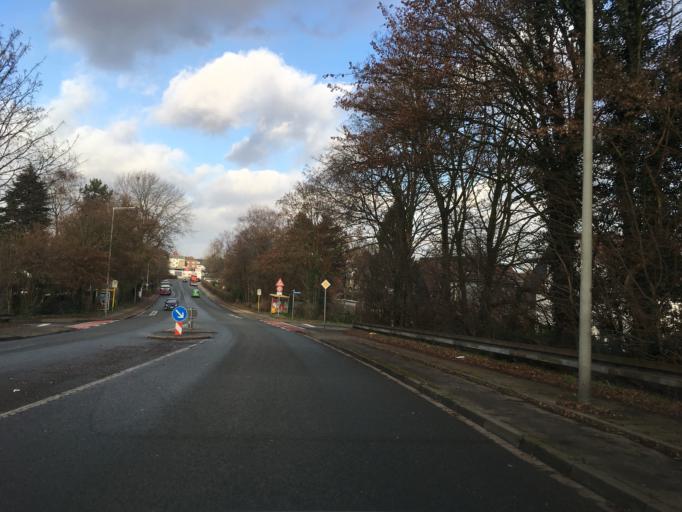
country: DE
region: North Rhine-Westphalia
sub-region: Regierungsbezirk Dusseldorf
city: Oberhausen
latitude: 51.5059
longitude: 6.8358
